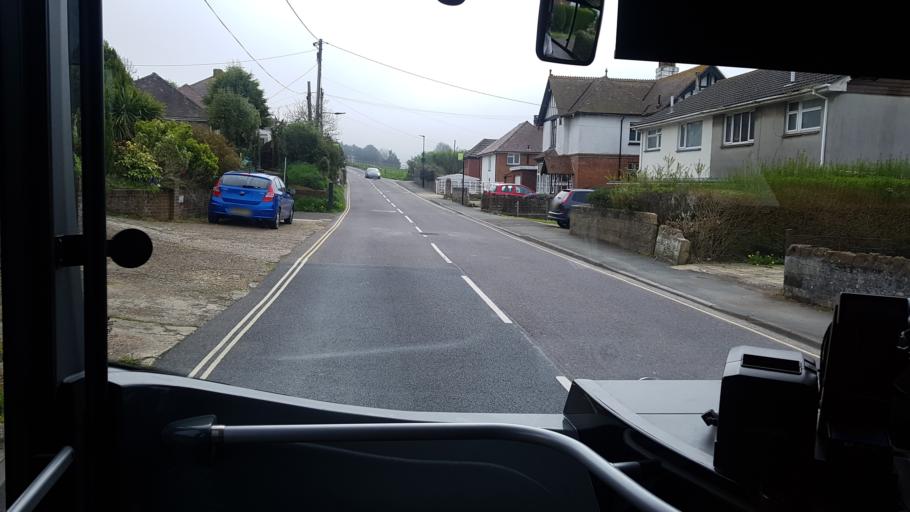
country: GB
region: England
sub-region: Isle of Wight
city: Ventnor
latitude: 50.6120
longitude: -1.2244
